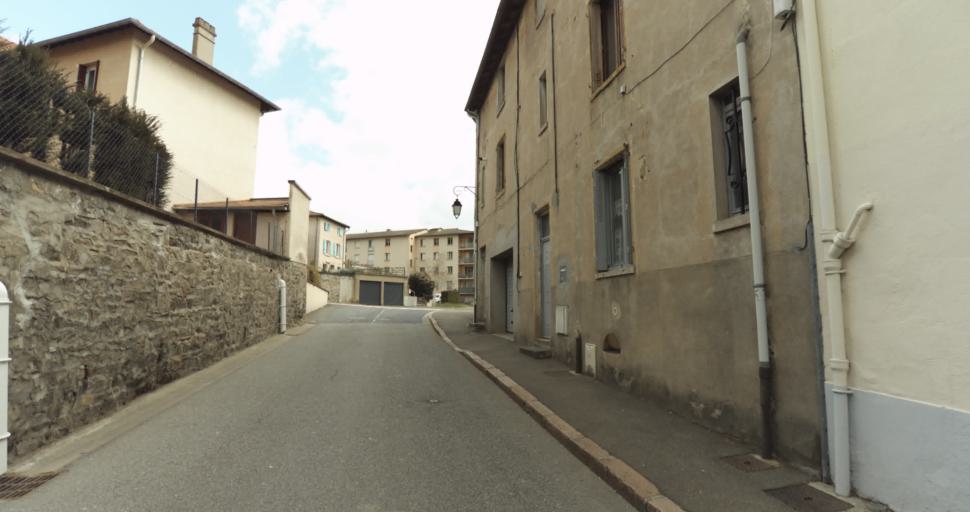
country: FR
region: Rhone-Alpes
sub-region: Departement du Rhone
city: Tarare
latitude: 45.8970
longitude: 4.4286
